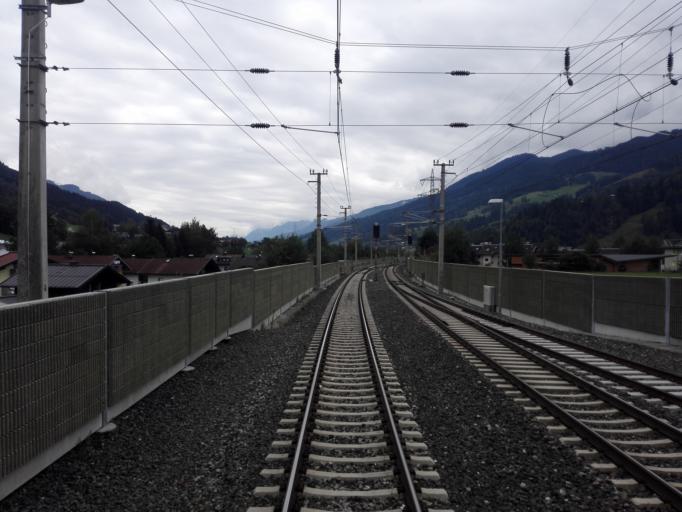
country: AT
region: Salzburg
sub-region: Politischer Bezirk Zell am See
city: Bruck an der Grossglocknerstrasse
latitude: 47.2845
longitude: 12.8317
